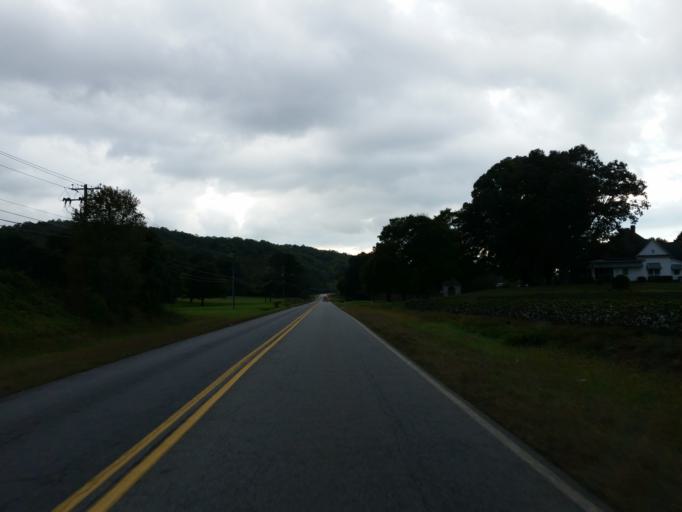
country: US
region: Georgia
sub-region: Bartow County
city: Cartersville
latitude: 34.1169
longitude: -84.8063
